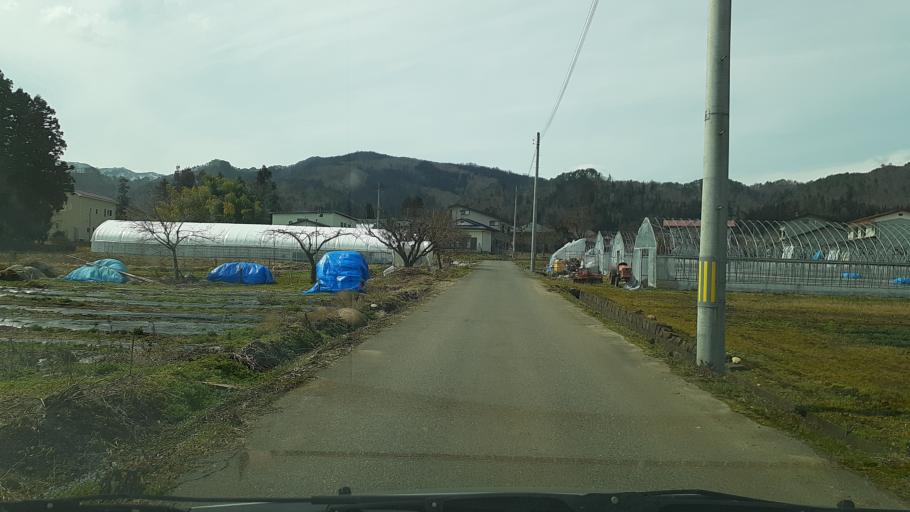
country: JP
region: Fukushima
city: Kitakata
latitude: 37.4635
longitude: 139.8157
